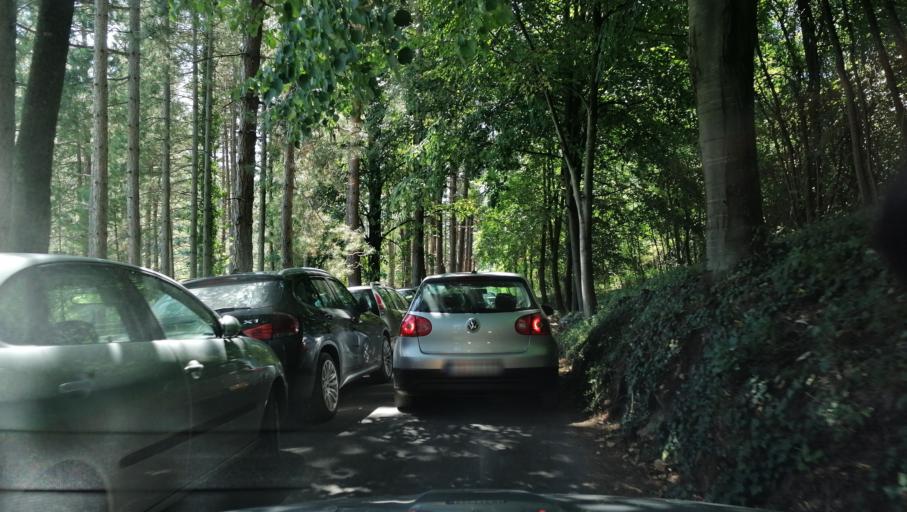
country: RS
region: Central Serbia
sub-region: Kolubarski Okrug
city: Valjevo
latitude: 44.2360
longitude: 19.8655
